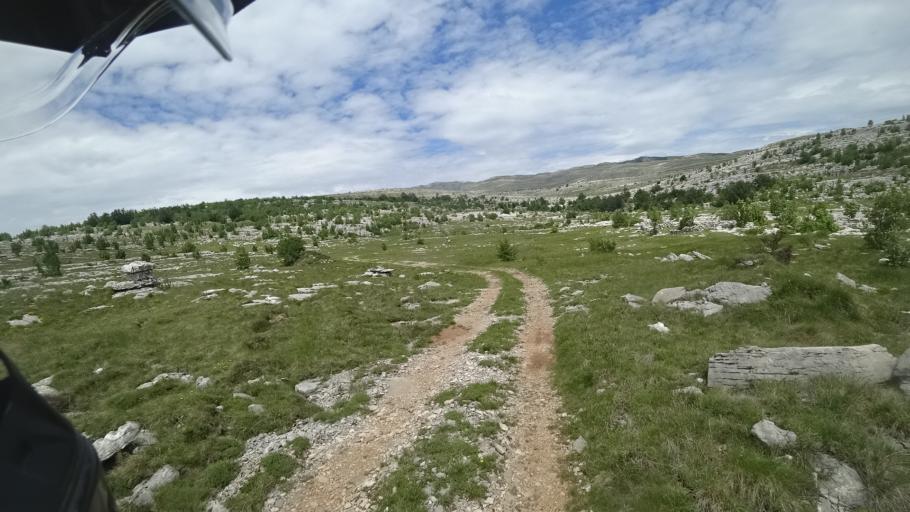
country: HR
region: Splitsko-Dalmatinska
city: Hrvace
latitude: 43.8919
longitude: 16.5851
